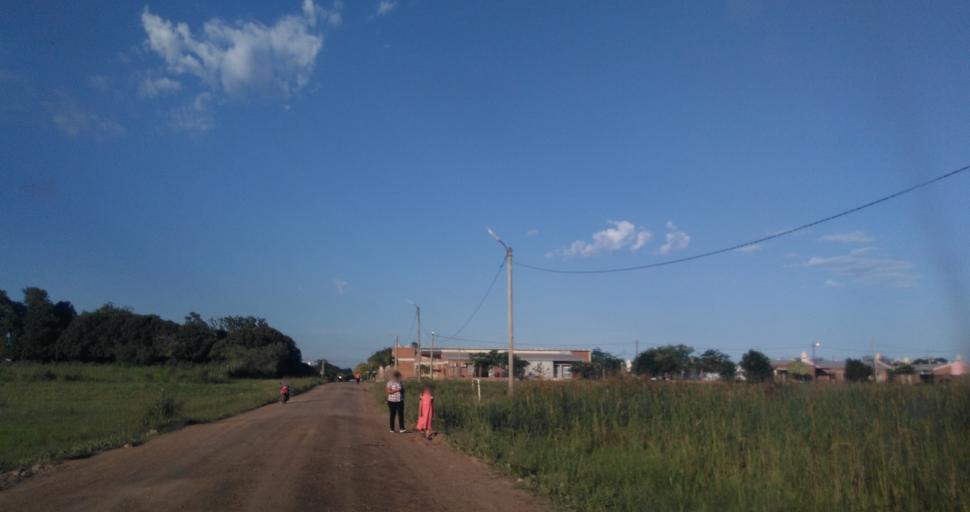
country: AR
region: Chaco
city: Fontana
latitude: -27.4148
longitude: -59.0271
